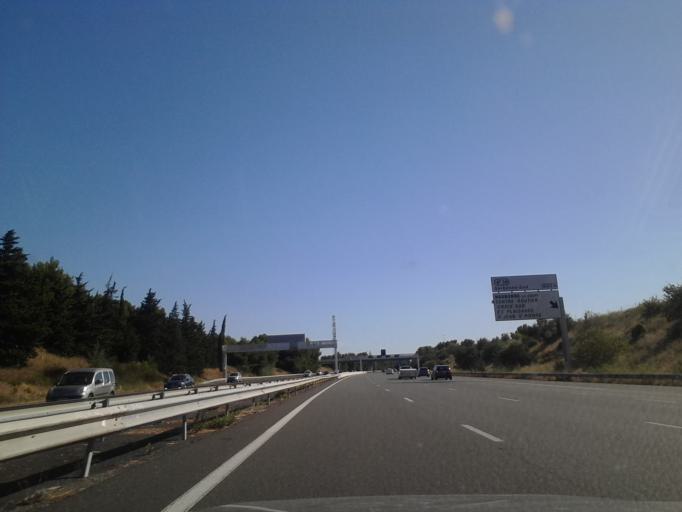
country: FR
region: Languedoc-Roussillon
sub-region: Departement de l'Aude
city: Narbonne
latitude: 43.1573
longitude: 2.9879
